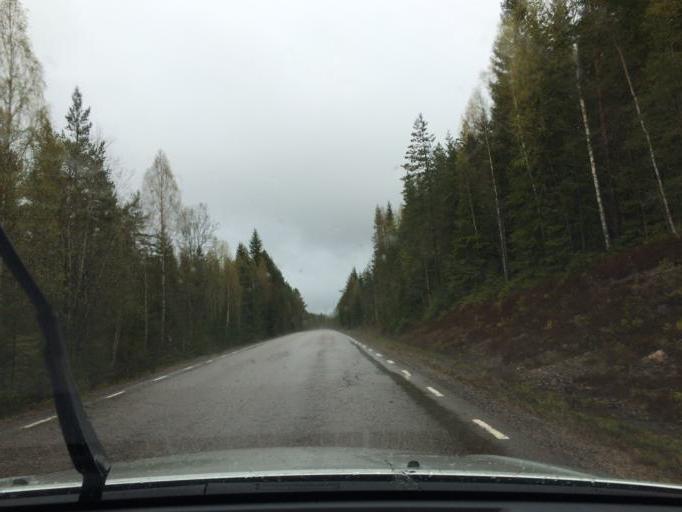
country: SE
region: Dalarna
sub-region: Ludvika Kommun
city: Abborrberget
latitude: 60.0520
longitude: 14.7930
